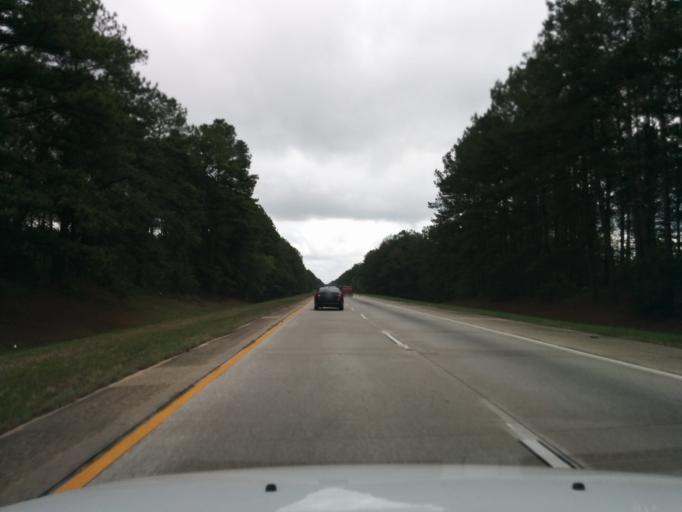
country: US
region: Georgia
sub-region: Evans County
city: Claxton
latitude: 32.2973
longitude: -81.8272
